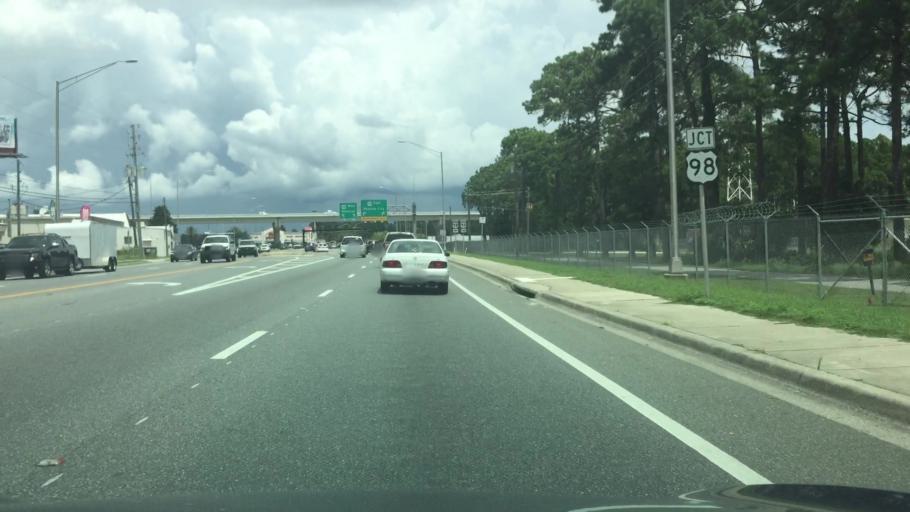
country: US
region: Florida
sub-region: Bay County
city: Upper Grand Lagoon
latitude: 30.1856
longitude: -85.7608
